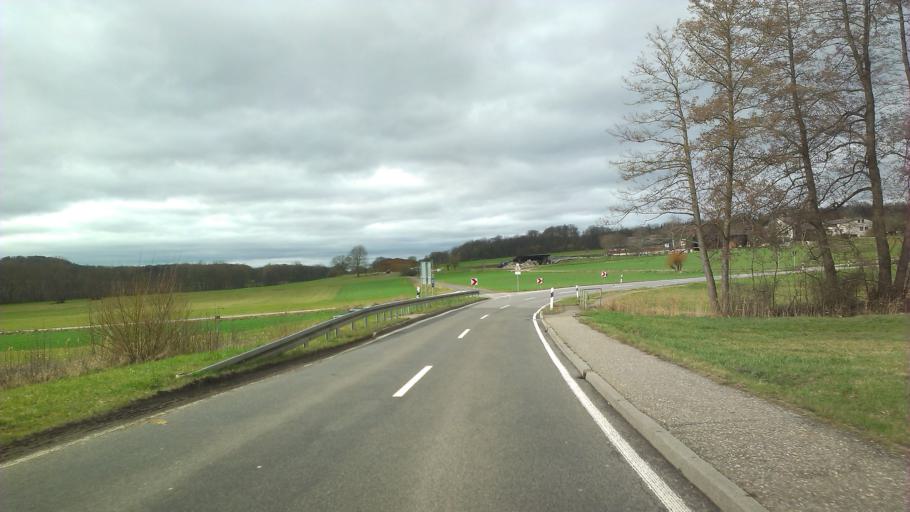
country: DE
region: Baden-Wuerttemberg
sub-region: Karlsruhe Region
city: Illingen
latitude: 48.9611
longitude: 8.9100
